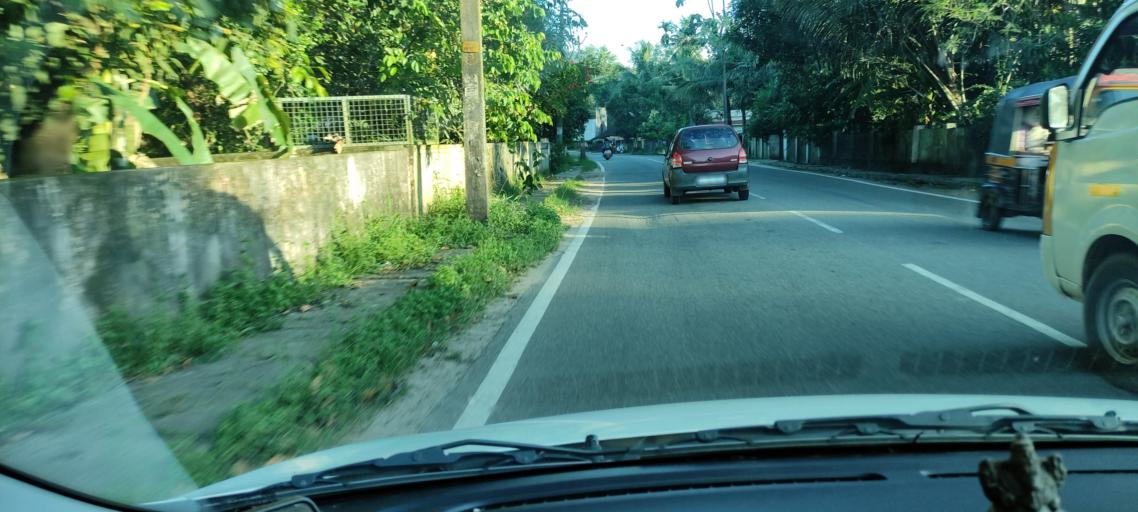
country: IN
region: Kerala
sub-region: Pattanamtitta
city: Adur
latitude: 9.1437
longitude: 76.7755
